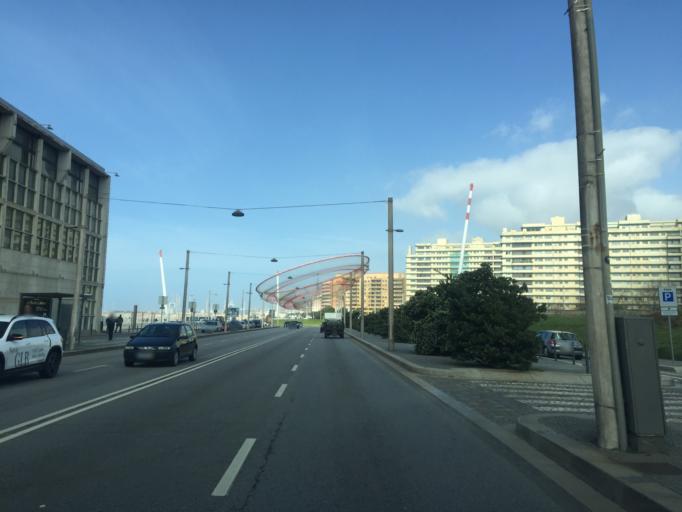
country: PT
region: Porto
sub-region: Matosinhos
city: Matosinhos
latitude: 41.1716
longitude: -8.6875
